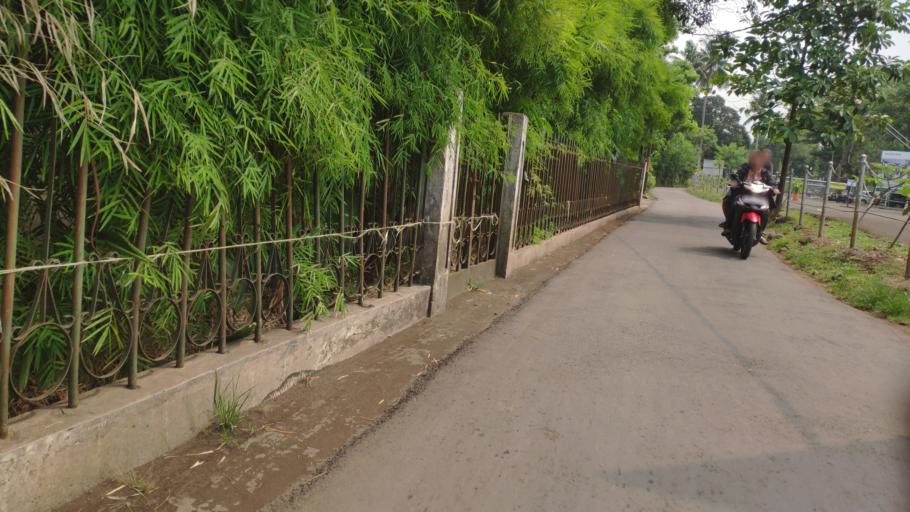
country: ID
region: West Java
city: Depok
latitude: -6.3386
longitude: 106.8178
